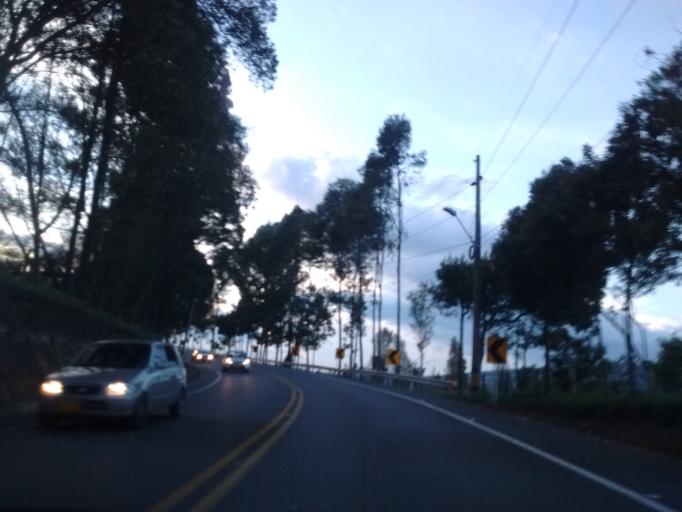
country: CO
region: Antioquia
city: Envigado
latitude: 6.1596
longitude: -75.5215
